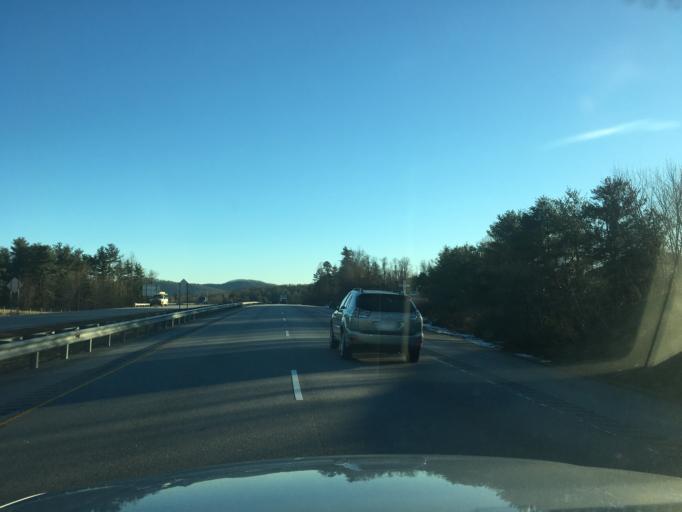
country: US
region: North Carolina
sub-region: Henderson County
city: East Flat Rock
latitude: 35.2746
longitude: -82.4018
